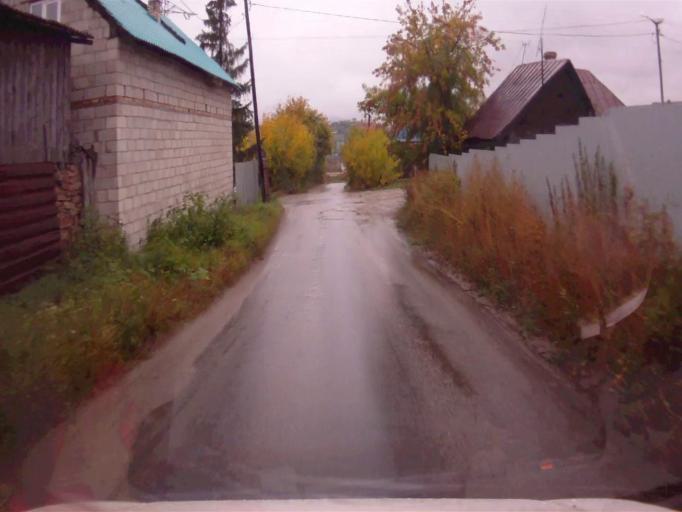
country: RU
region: Chelyabinsk
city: Kyshtym
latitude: 55.7147
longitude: 60.5508
